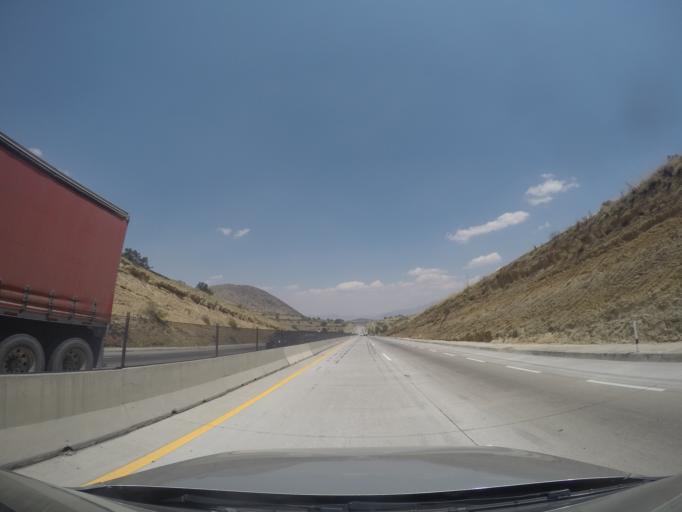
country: MX
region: Hidalgo
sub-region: Emiliano Zapata
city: Jose Maria Morelos (San Jose)
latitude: 19.6859
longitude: -98.5928
